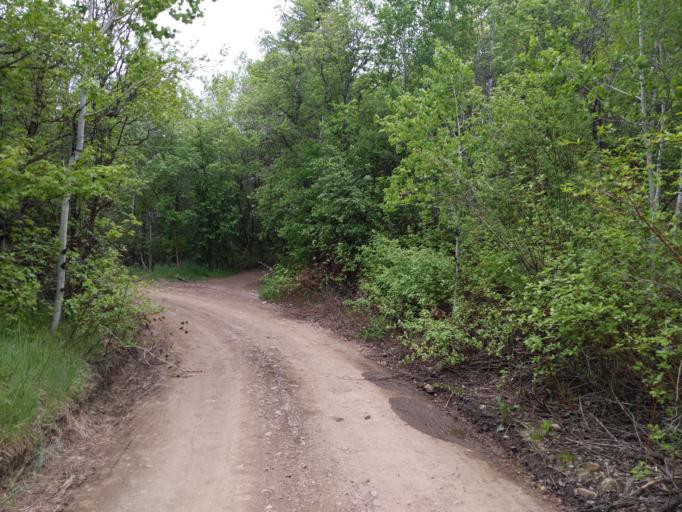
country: US
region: Idaho
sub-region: Bannock County
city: Pocatello
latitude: 42.8253
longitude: -112.4847
